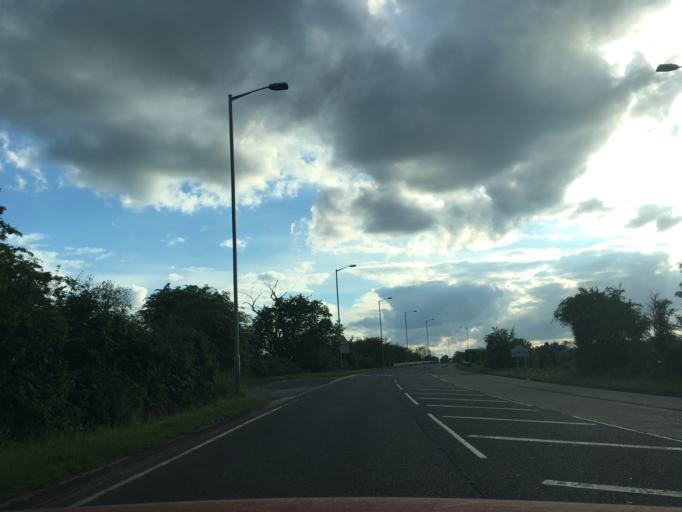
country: GB
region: England
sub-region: Worcestershire
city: Fernhill Heath
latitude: 52.1828
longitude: -2.1405
